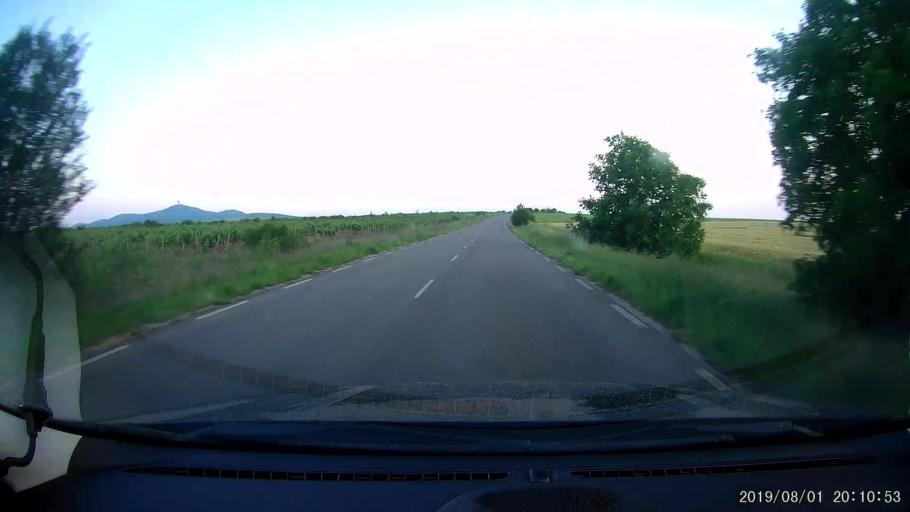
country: BG
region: Yambol
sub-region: Obshtina Yambol
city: Yambol
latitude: 42.4726
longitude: 26.6036
